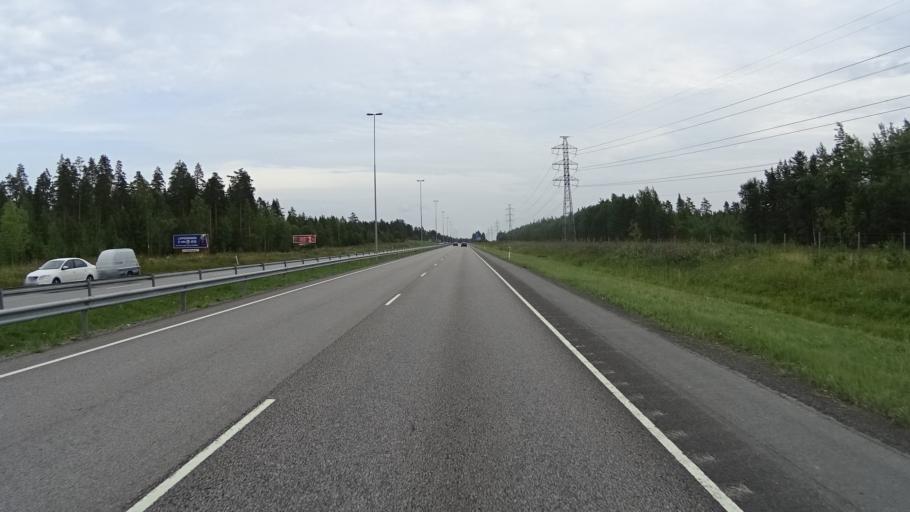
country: FI
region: South Karelia
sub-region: Lappeenranta
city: Lappeenranta
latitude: 61.0396
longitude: 28.1461
